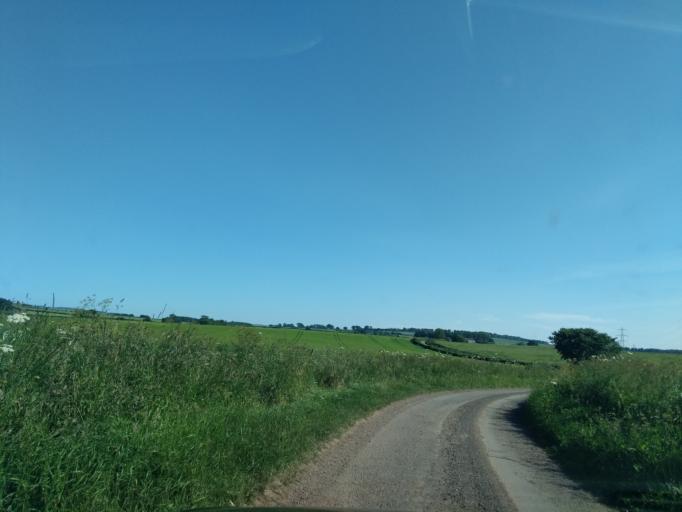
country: GB
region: Scotland
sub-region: East Lothian
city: Ormiston
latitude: 55.8852
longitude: -2.9361
